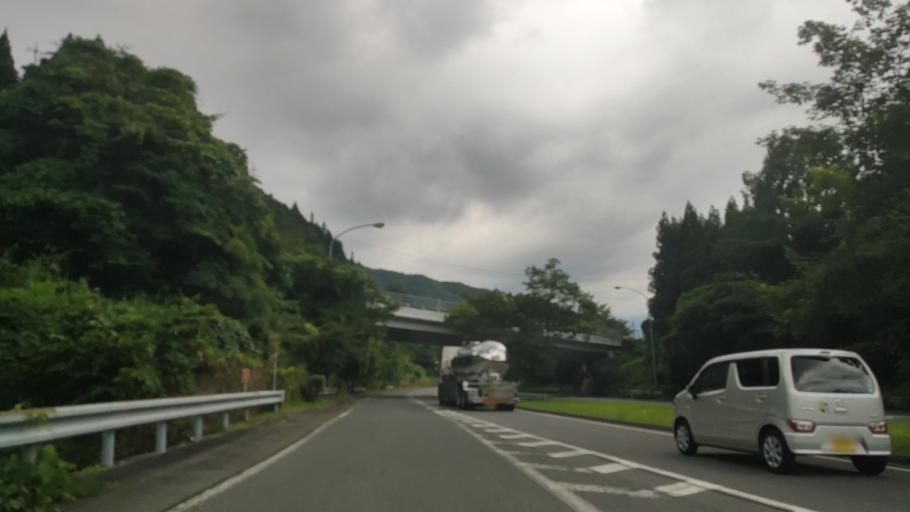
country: JP
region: Tochigi
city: Nikko
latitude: 36.7405
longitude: 139.6257
